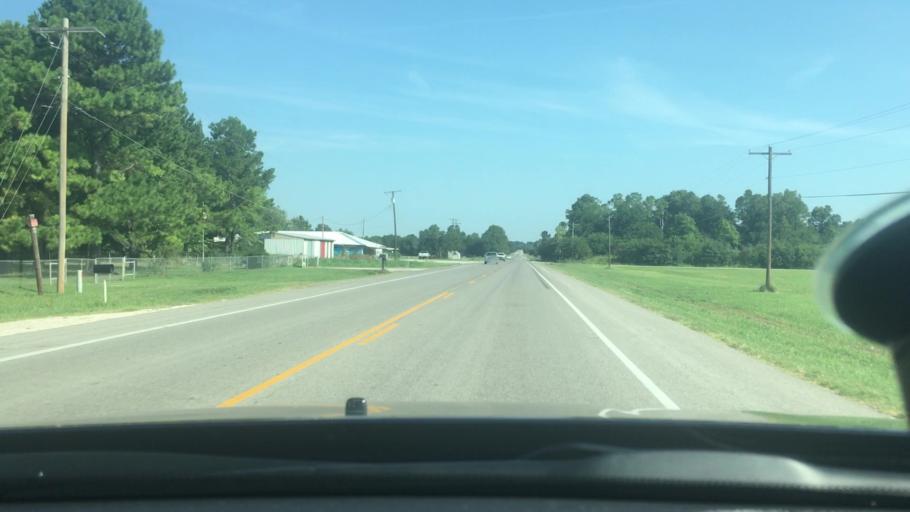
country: US
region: Oklahoma
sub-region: Garvin County
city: Wynnewood
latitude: 34.6643
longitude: -97.2042
